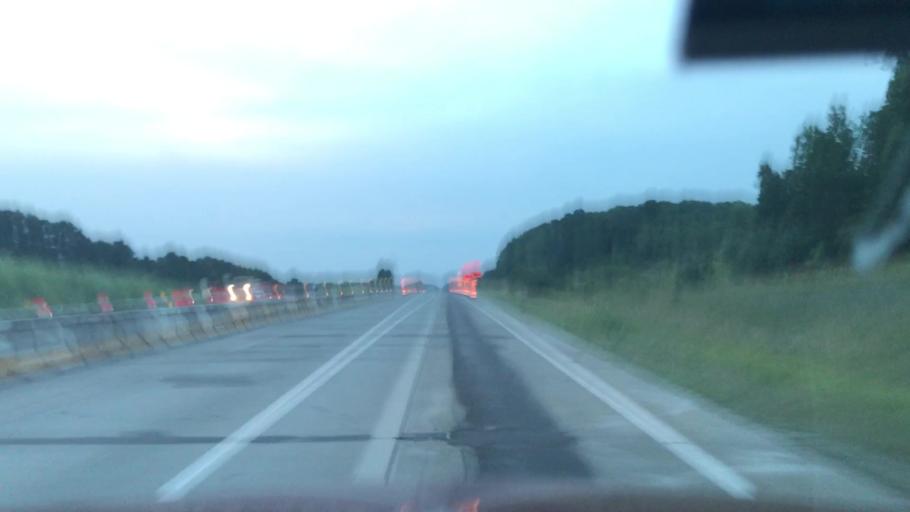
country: US
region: Michigan
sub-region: Kent County
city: Cedar Springs
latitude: 43.1768
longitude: -85.5750
